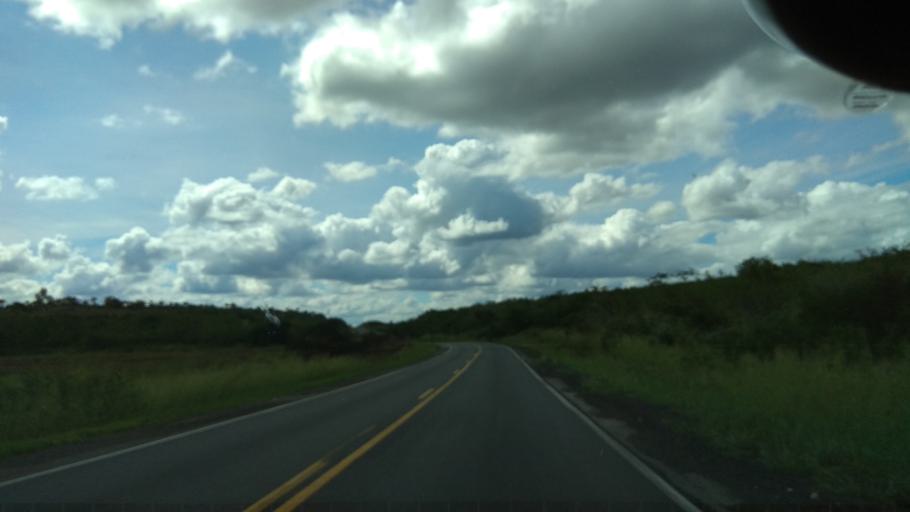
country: BR
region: Bahia
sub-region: Jaguaquara
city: Jaguaquara
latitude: -13.4609
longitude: -40.0336
